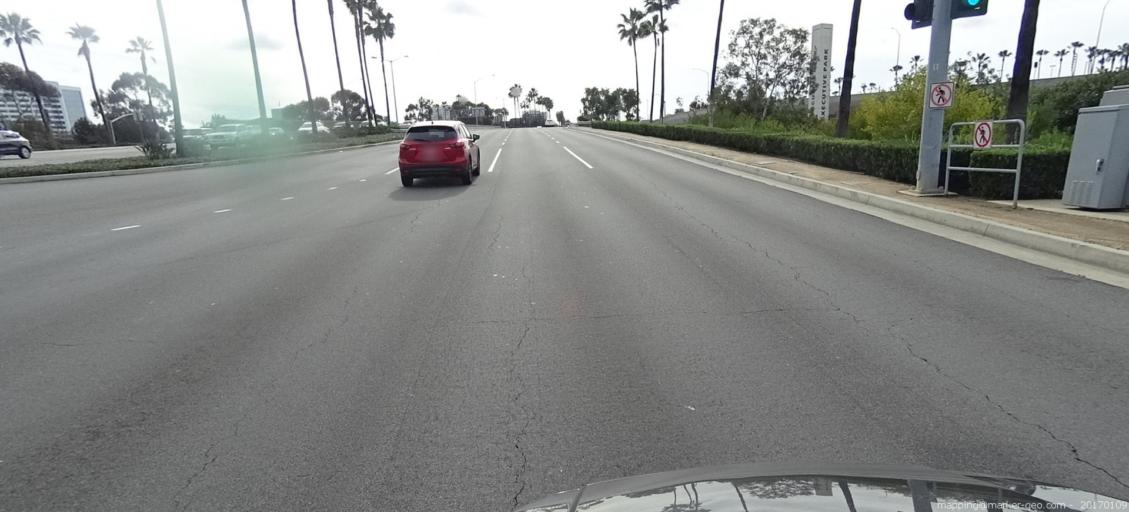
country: US
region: California
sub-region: Orange County
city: Irvine
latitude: 33.6840
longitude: -117.8565
